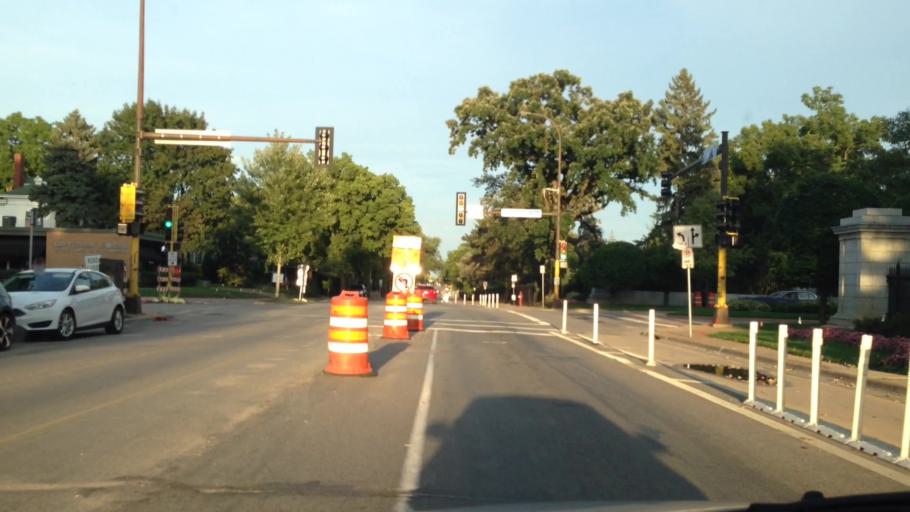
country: US
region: Minnesota
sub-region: Hennepin County
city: Saint Louis Park
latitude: 44.9377
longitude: -93.2990
